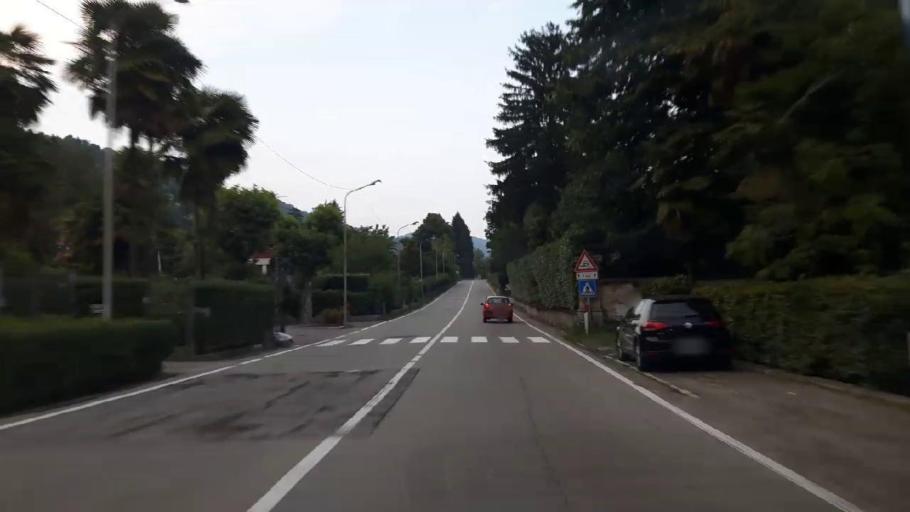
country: IT
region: Piedmont
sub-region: Provincia di Novara
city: Meina
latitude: 45.7992
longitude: 8.5374
